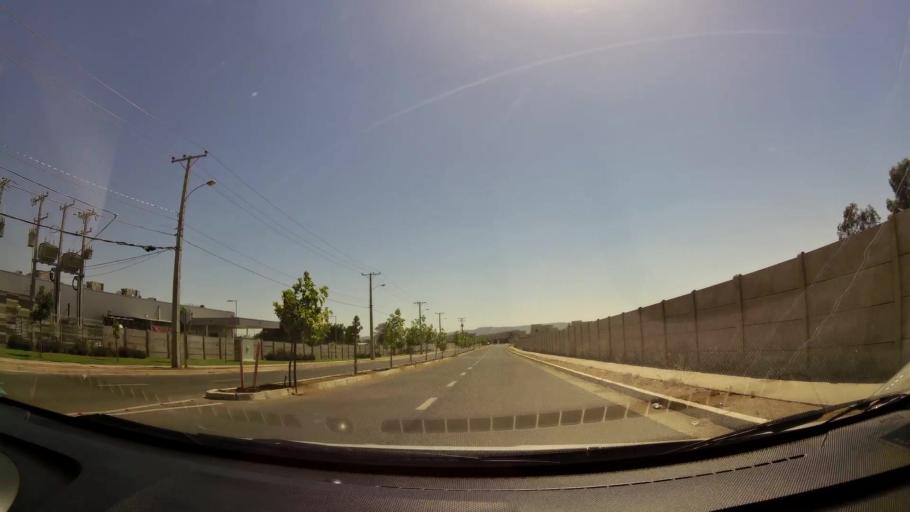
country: CL
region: Maule
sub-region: Provincia de Talca
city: Talca
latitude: -35.4312
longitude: -71.6082
